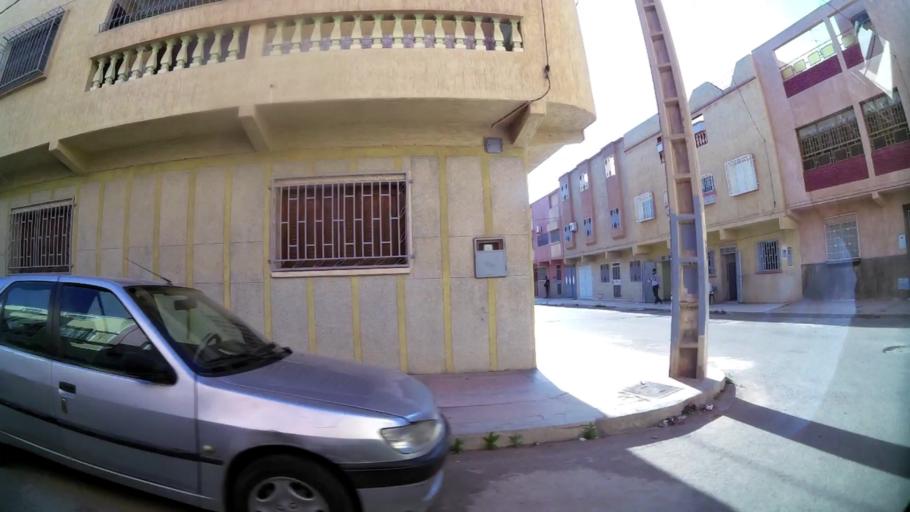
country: MA
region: Oriental
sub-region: Oujda-Angad
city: Oujda
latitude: 34.6957
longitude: -1.9122
